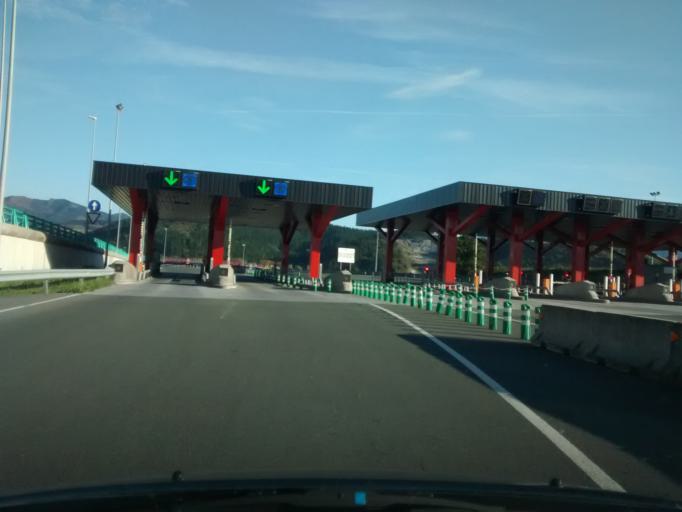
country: ES
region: Basque Country
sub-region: Bizkaia
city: Abadino
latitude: 43.1689
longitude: -2.6054
